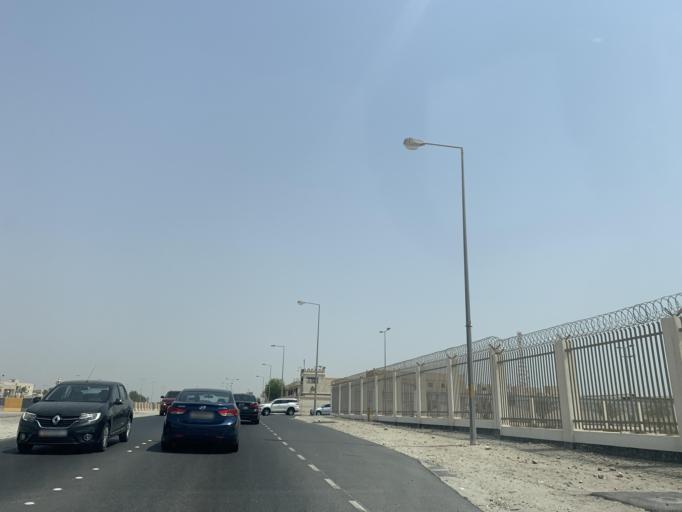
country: BH
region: Central Governorate
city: Madinat Hamad
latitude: 26.1575
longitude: 50.4781
